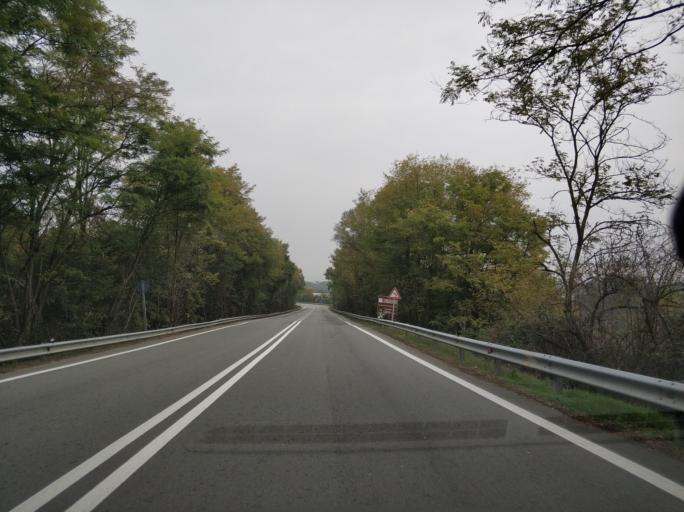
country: IT
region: Piedmont
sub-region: Provincia di Torino
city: Lombardore
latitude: 45.2278
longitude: 7.7473
